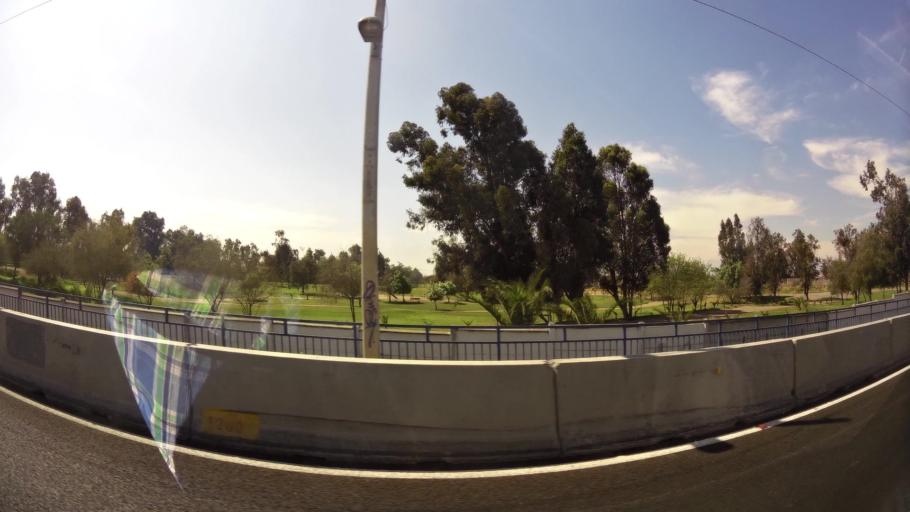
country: CL
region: Santiago Metropolitan
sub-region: Provincia de Santiago
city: Lo Prado
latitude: -33.4766
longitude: -70.7028
